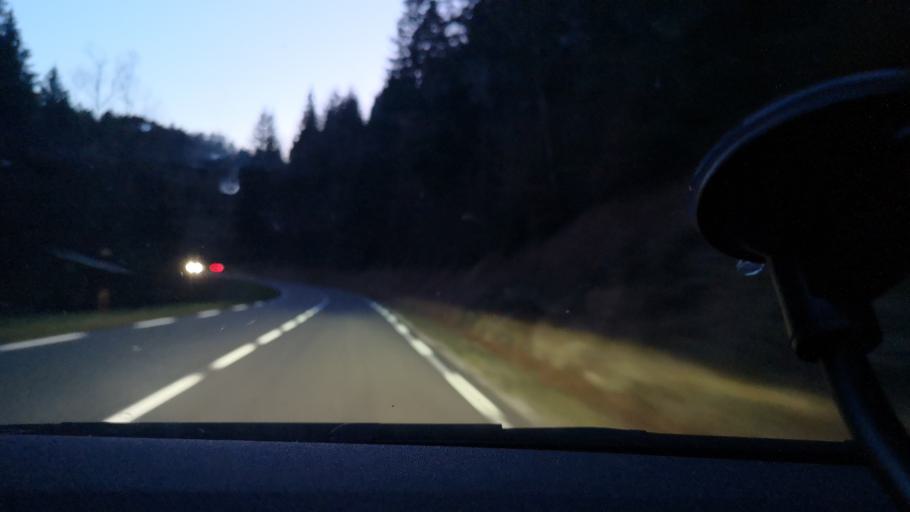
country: FR
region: Franche-Comte
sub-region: Departement du Jura
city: Champagnole
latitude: 46.7659
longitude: 5.9794
